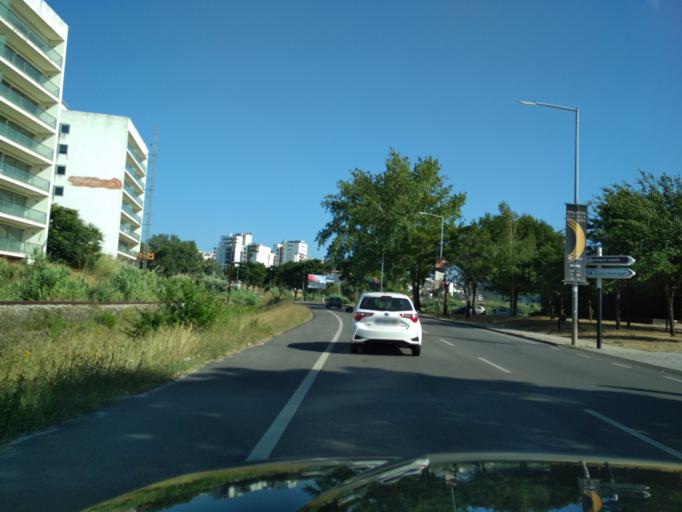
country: PT
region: Coimbra
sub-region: Coimbra
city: Coimbra
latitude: 40.2001
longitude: -8.4234
